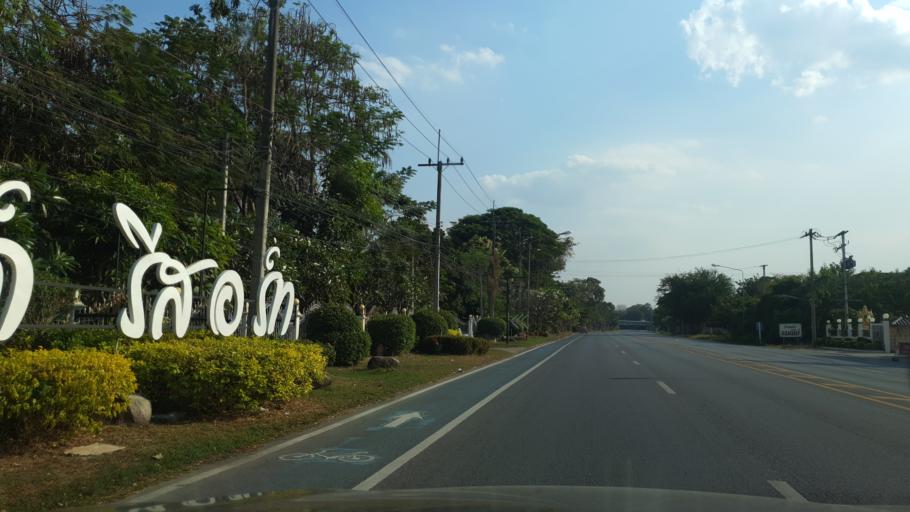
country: TH
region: Tak
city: Tak
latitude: 16.8611
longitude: 99.1212
